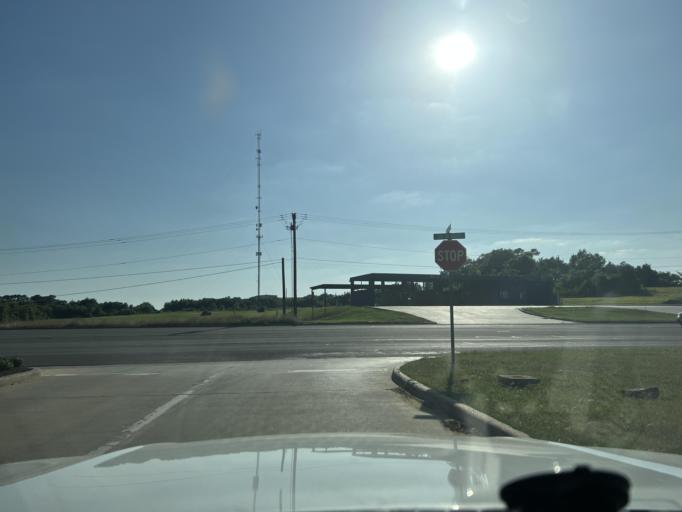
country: US
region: Texas
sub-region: Washington County
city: Brenham
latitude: 30.1374
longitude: -96.3953
